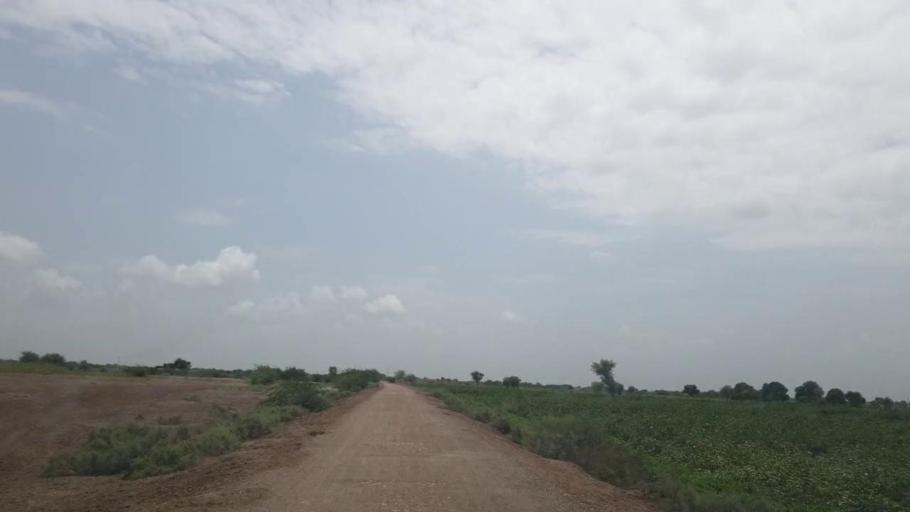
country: PK
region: Sindh
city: Naukot
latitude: 24.9031
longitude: 69.2029
